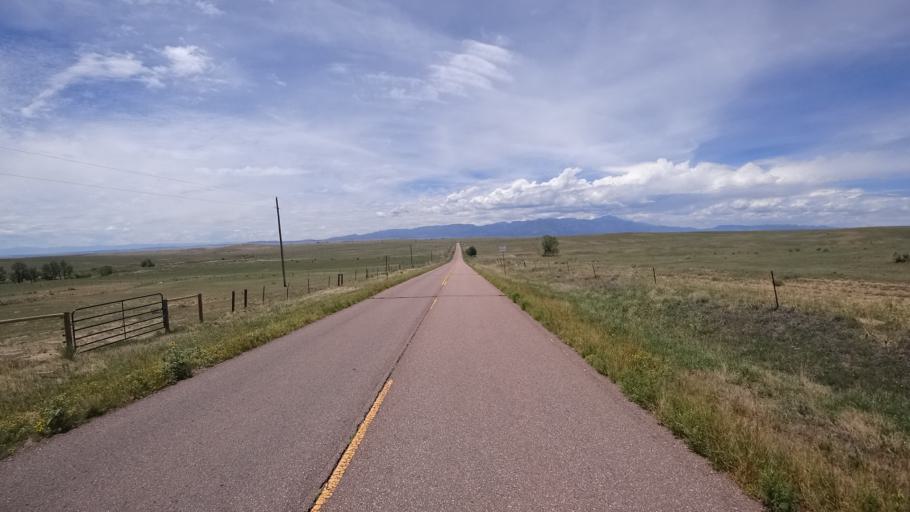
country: US
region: Colorado
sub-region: El Paso County
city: Fountain
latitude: 38.6940
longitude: -104.5985
